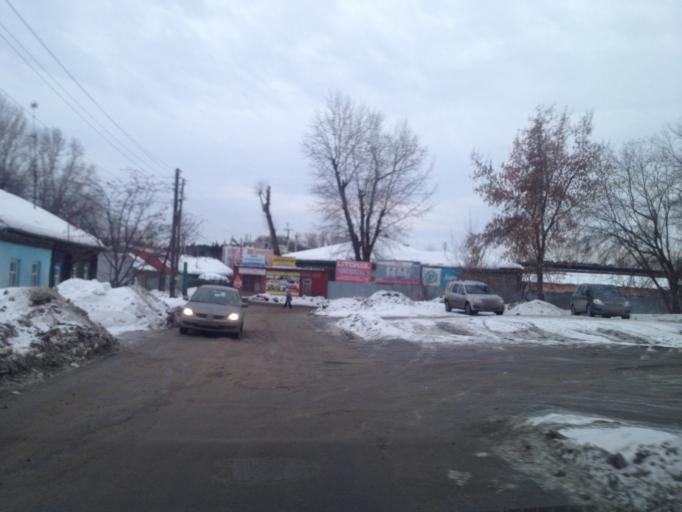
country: RU
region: Sverdlovsk
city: Yekaterinburg
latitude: 56.7999
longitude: 60.5984
